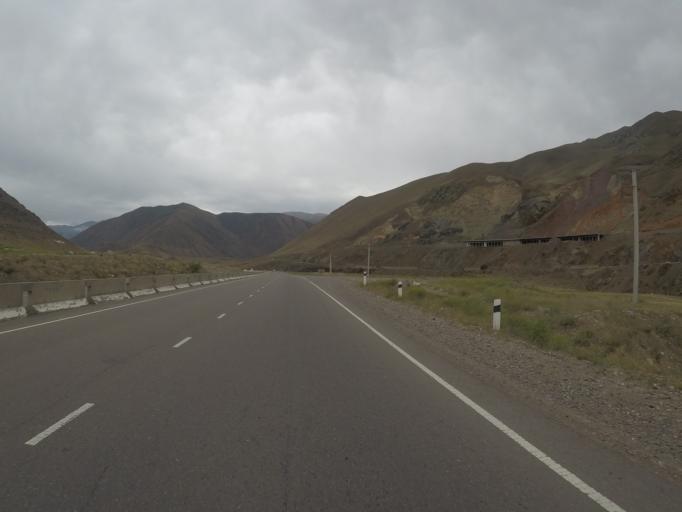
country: KG
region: Chuy
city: Bystrovka
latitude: 42.6967
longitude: 75.8709
